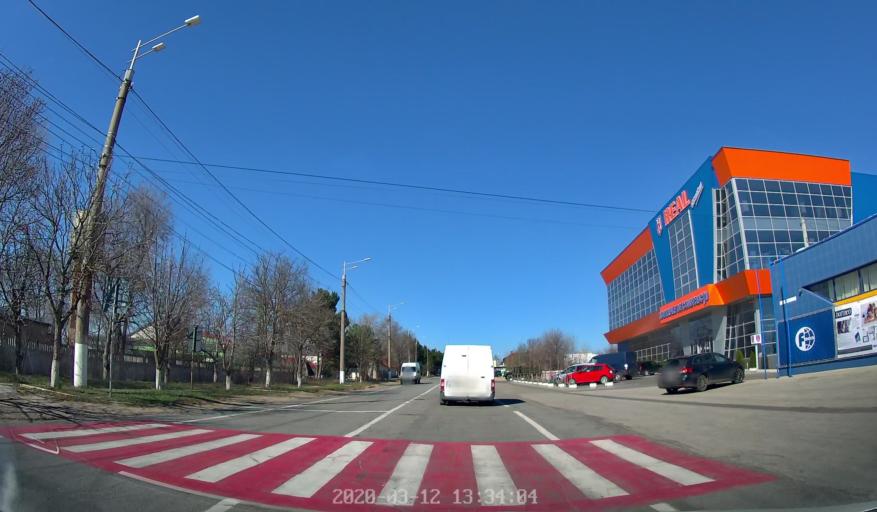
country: MD
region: Laloveni
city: Ialoveni
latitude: 46.9609
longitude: 28.7677
